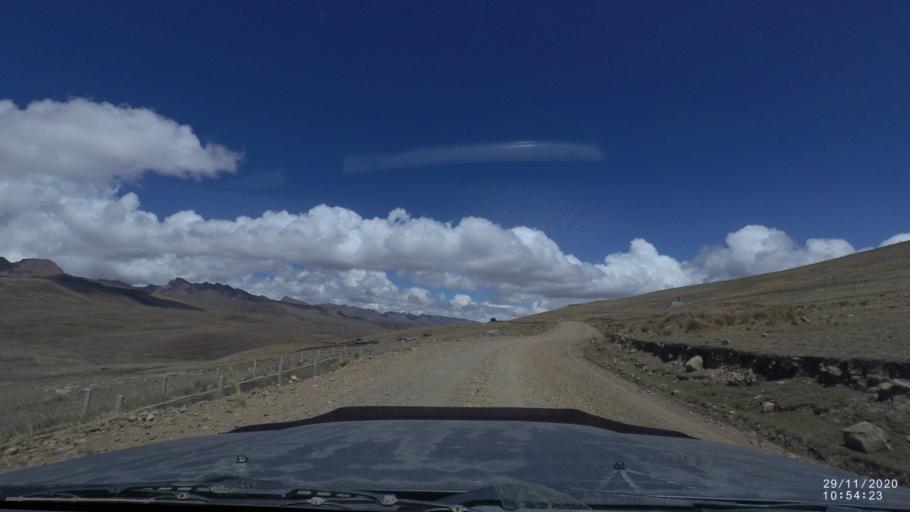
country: BO
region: Cochabamba
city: Cochabamba
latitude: -17.2285
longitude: -66.2193
